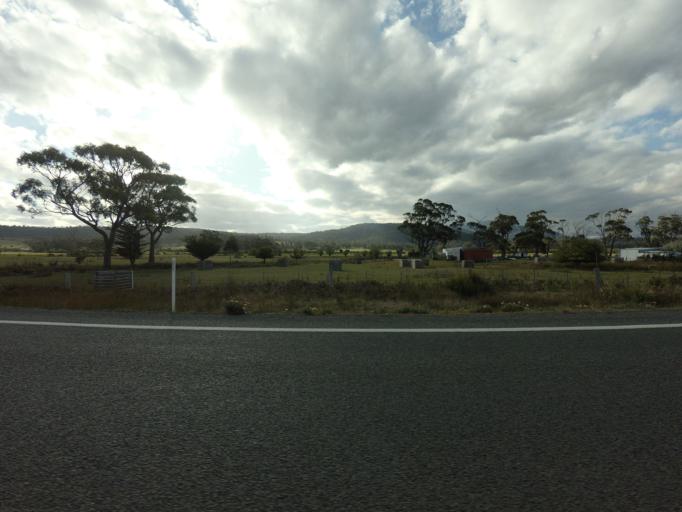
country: AU
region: Tasmania
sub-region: Sorell
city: Sorell
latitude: -42.6483
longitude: 147.5545
